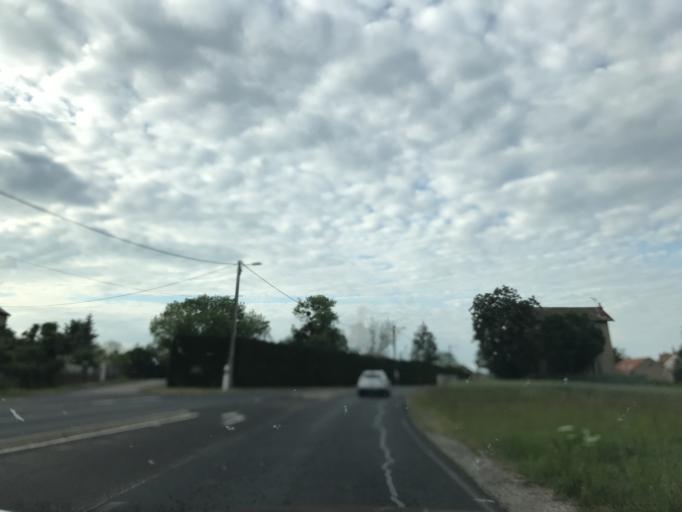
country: FR
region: Auvergne
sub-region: Departement du Puy-de-Dome
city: Randan
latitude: 46.0405
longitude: 3.3605
